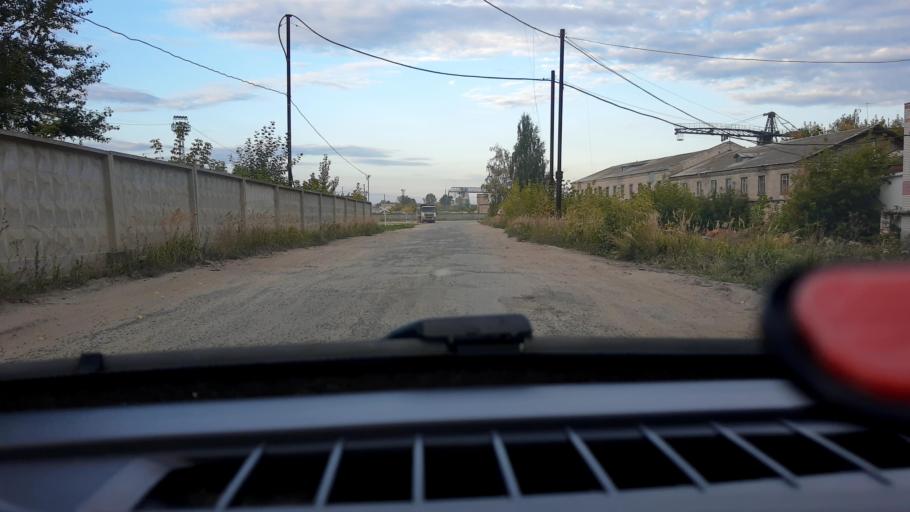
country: RU
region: Nizjnij Novgorod
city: Nizhniy Novgorod
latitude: 56.2357
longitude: 43.9152
